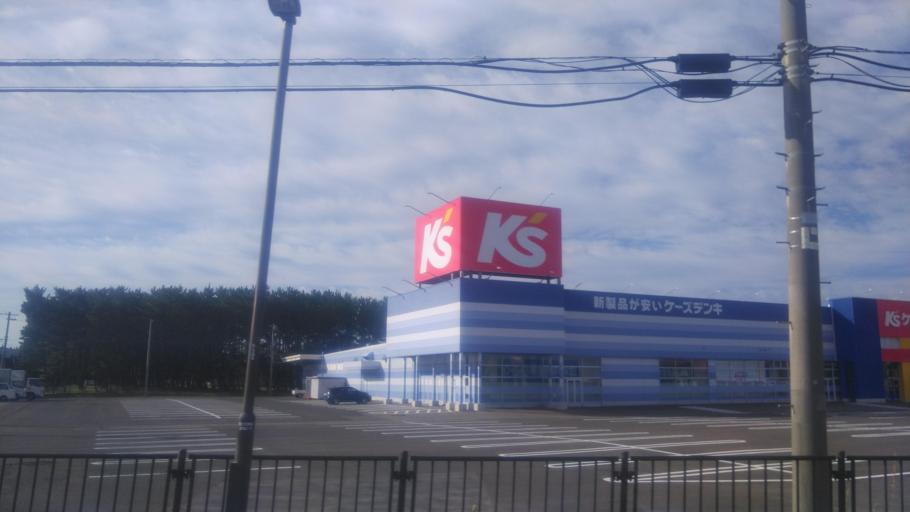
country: JP
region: Akita
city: Noshiromachi
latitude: 40.1855
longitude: 140.0487
